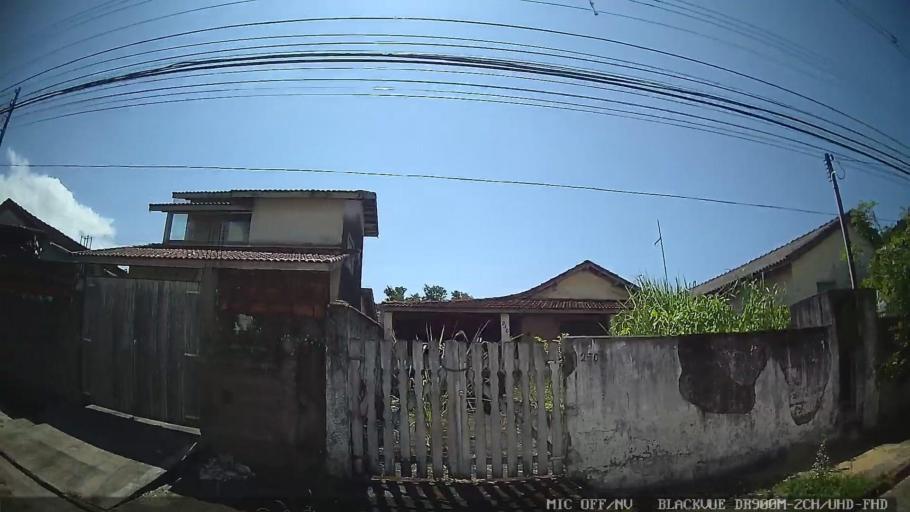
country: BR
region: Sao Paulo
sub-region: Peruibe
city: Peruibe
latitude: -24.3249
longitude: -47.0039
